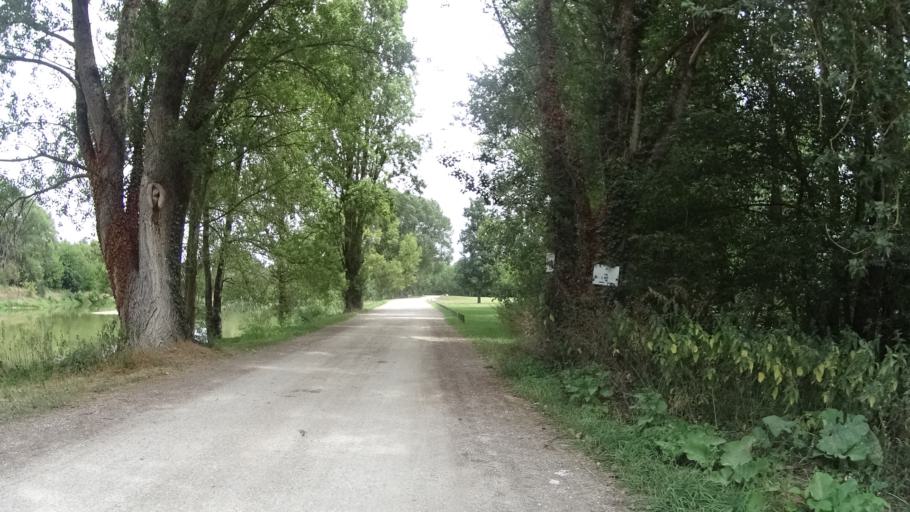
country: FR
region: Centre
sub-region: Departement du Loiret
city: Baule
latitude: 47.7888
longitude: 1.6567
